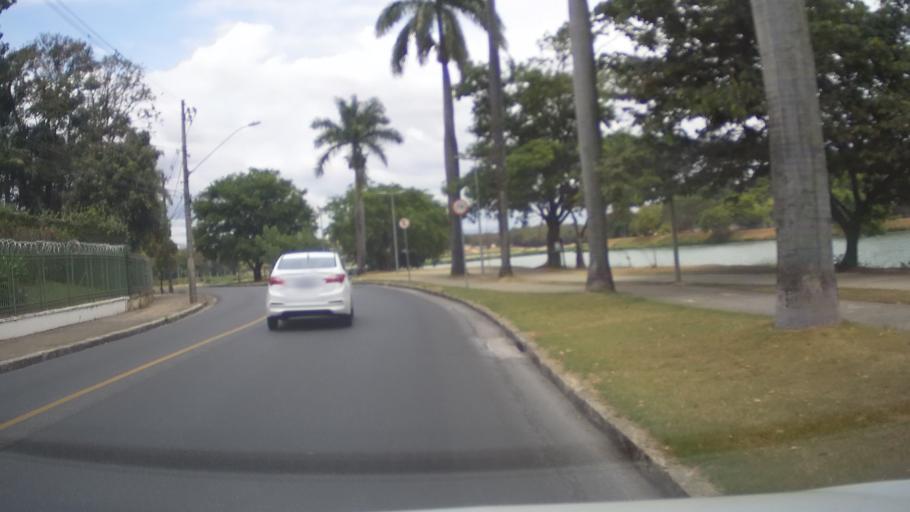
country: BR
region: Minas Gerais
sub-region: Belo Horizonte
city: Belo Horizonte
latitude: -19.8417
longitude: -43.9932
